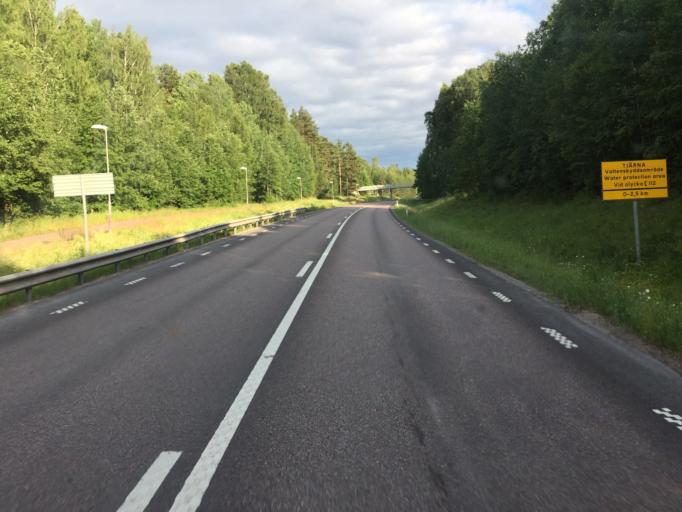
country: SE
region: Dalarna
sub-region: Borlange Kommun
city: Borlaenge
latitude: 60.5130
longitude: 15.3791
